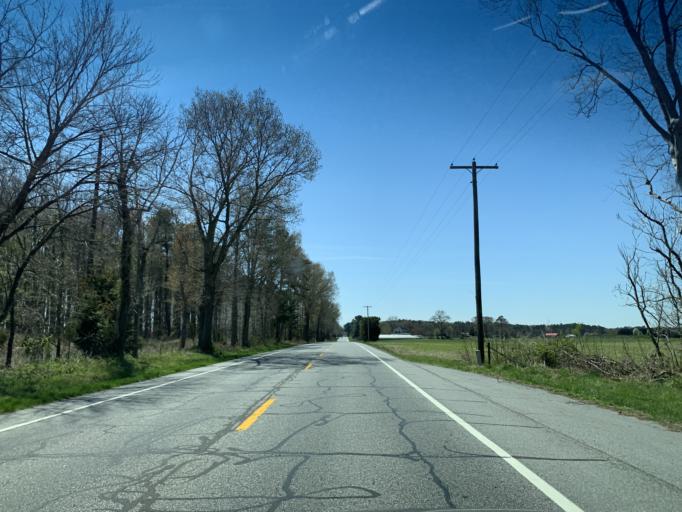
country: US
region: Maryland
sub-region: Talbot County
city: Easton
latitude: 38.8580
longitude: -76.0106
